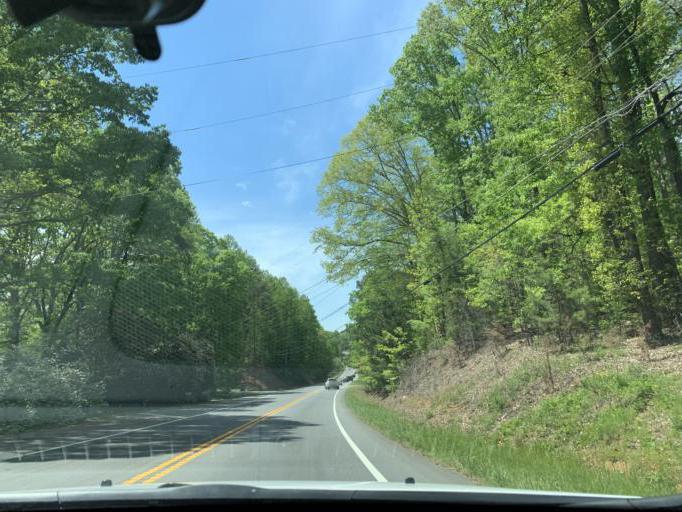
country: US
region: Georgia
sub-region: Hall County
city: Flowery Branch
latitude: 34.2461
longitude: -84.0231
